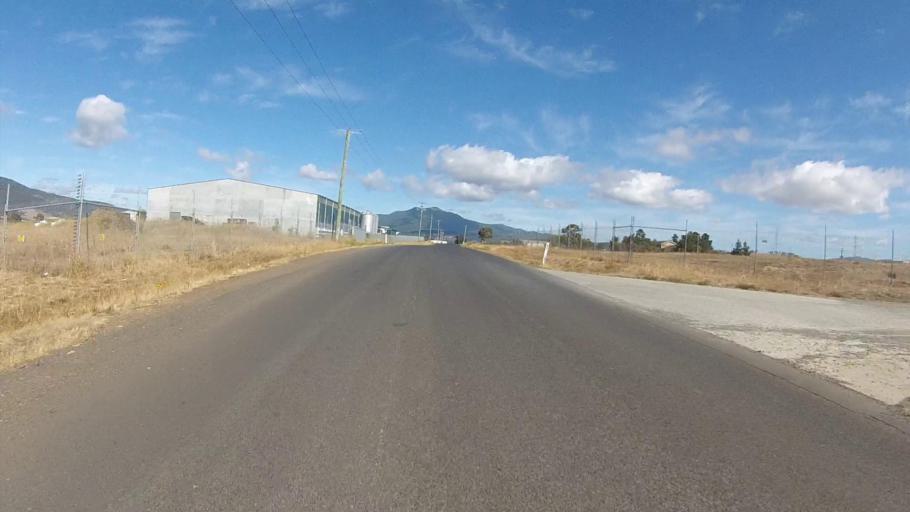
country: AU
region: Tasmania
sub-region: Brighton
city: Bridgewater
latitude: -42.7355
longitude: 147.2563
